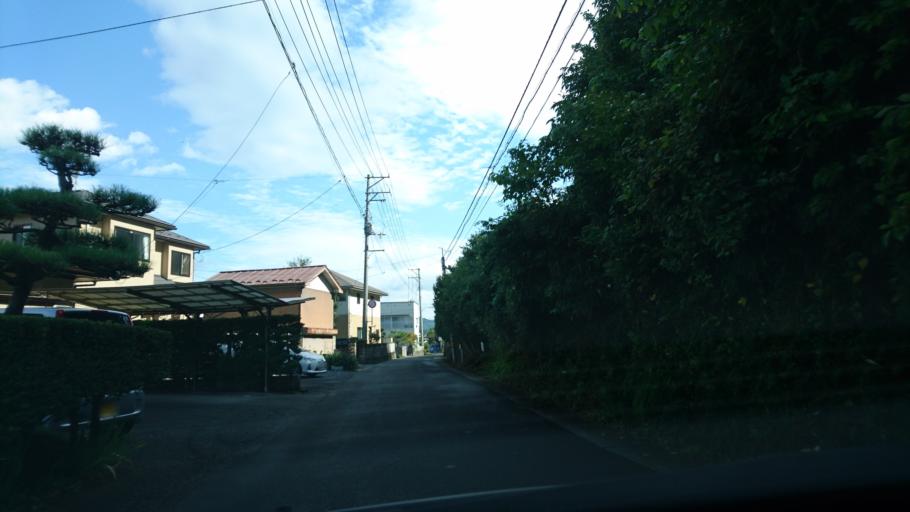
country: JP
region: Iwate
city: Ichinoseki
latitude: 38.9257
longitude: 141.1512
